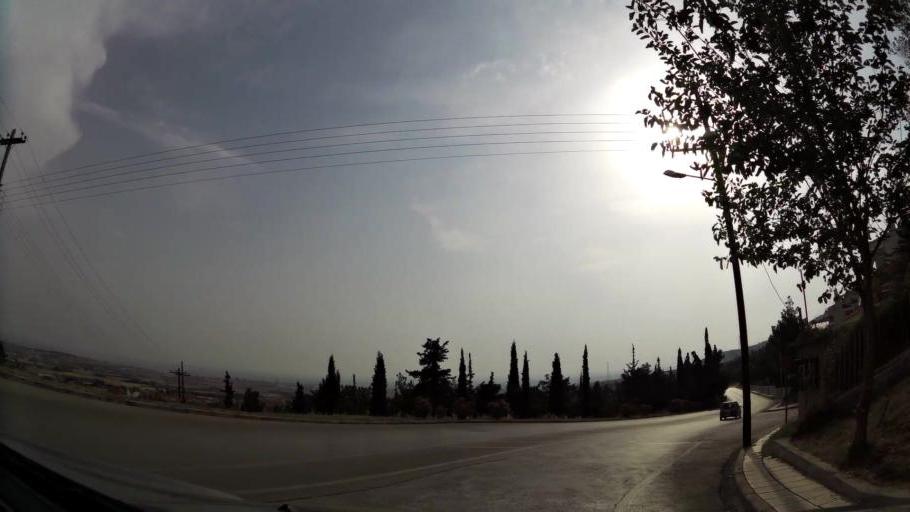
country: GR
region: Central Macedonia
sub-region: Nomos Thessalonikis
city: Oraiokastro
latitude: 40.7240
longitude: 22.9132
